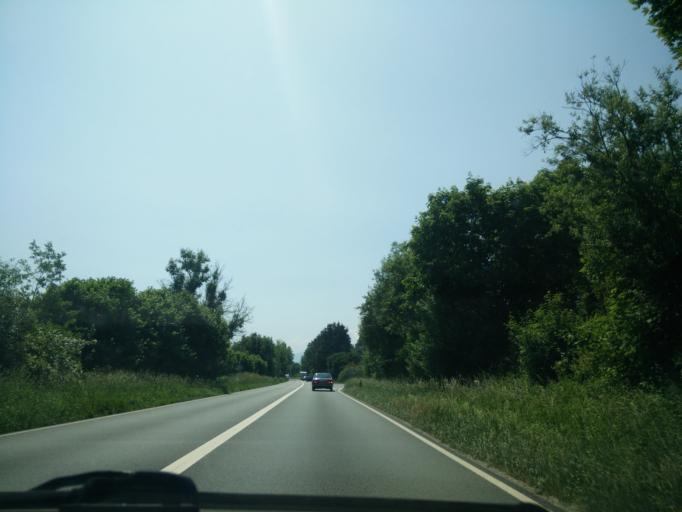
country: DE
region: Bavaria
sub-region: Upper Bavaria
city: Laufen
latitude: 47.9120
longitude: 12.9412
